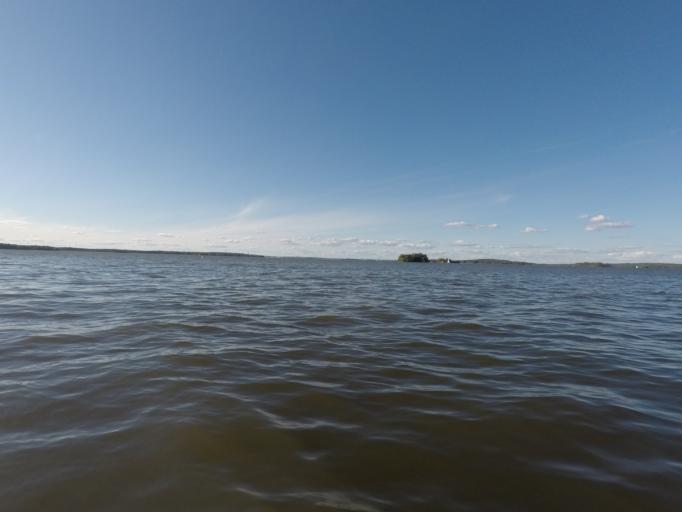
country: SE
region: Vaestmanland
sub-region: Vasteras
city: Vasteras
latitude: 59.5173
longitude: 16.5881
